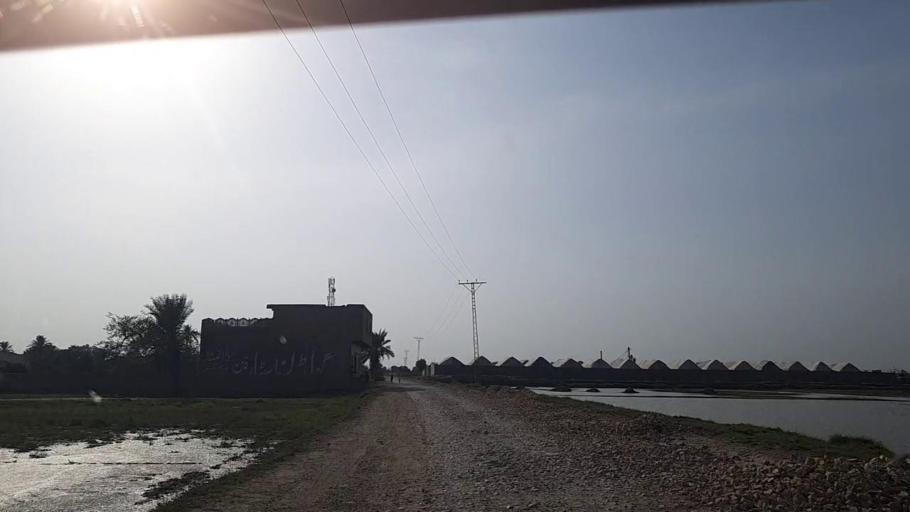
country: PK
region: Sindh
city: Ghotki
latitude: 28.0155
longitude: 69.2959
